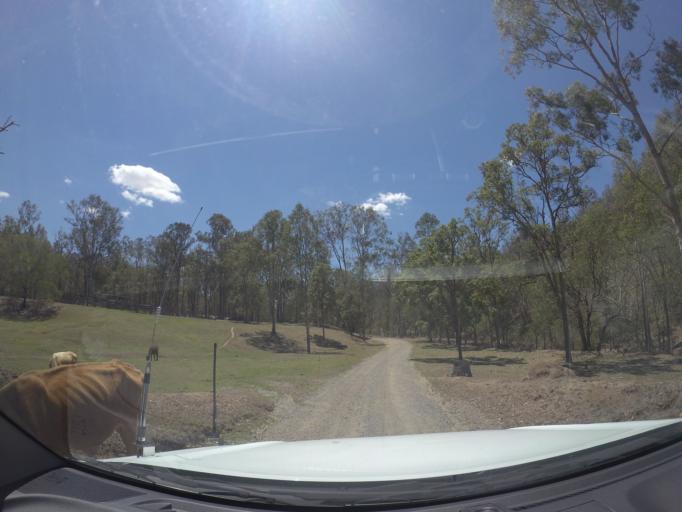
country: AU
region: Queensland
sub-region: Ipswich
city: Deebing Heights
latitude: -27.7597
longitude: 152.8105
